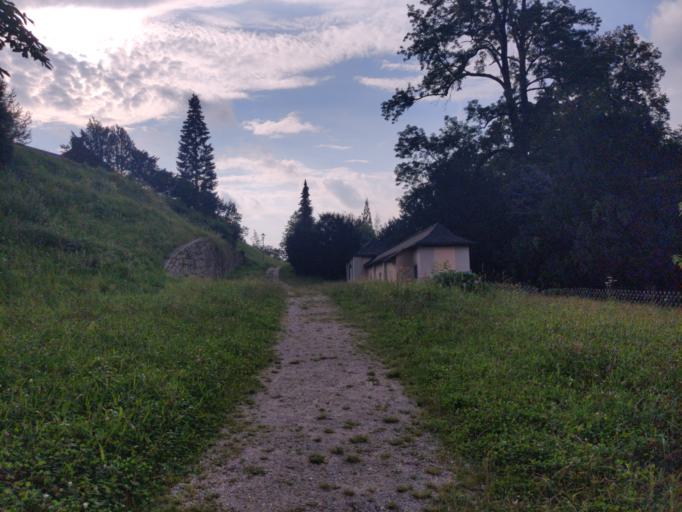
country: AT
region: Upper Austria
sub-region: Politischer Bezirk Perg
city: Bad Kreuzen
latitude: 48.2270
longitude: 14.8533
